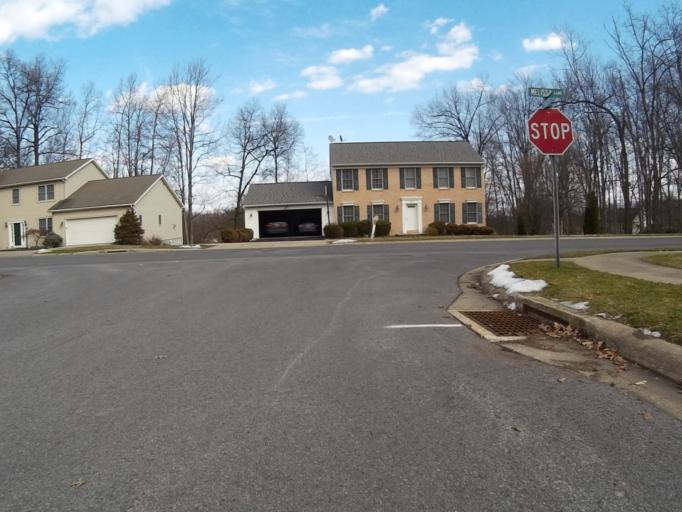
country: US
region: Pennsylvania
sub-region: Centre County
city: Park Forest Village
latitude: 40.7991
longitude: -77.9144
